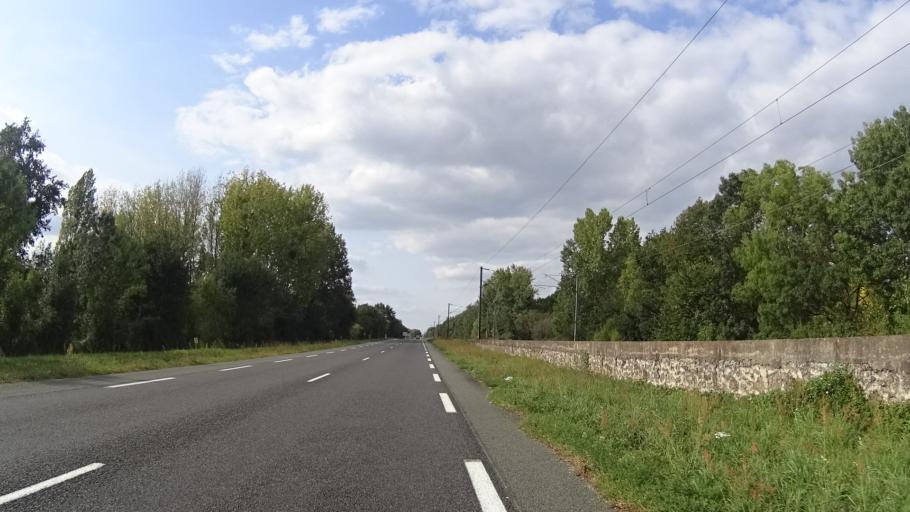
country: FR
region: Pays de la Loire
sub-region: Departement de Maine-et-Loire
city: Saint-Martin-de-la-Place
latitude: 47.2977
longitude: -0.1177
